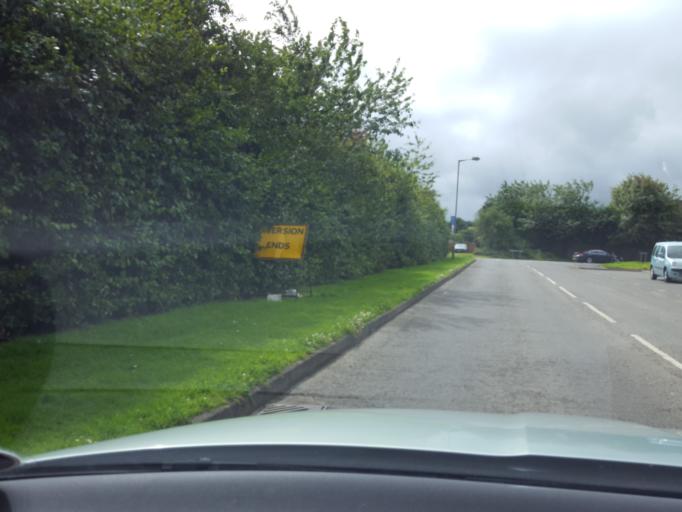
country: GB
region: Scotland
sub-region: Falkirk
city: Bo'ness
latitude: 56.0065
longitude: -3.6003
